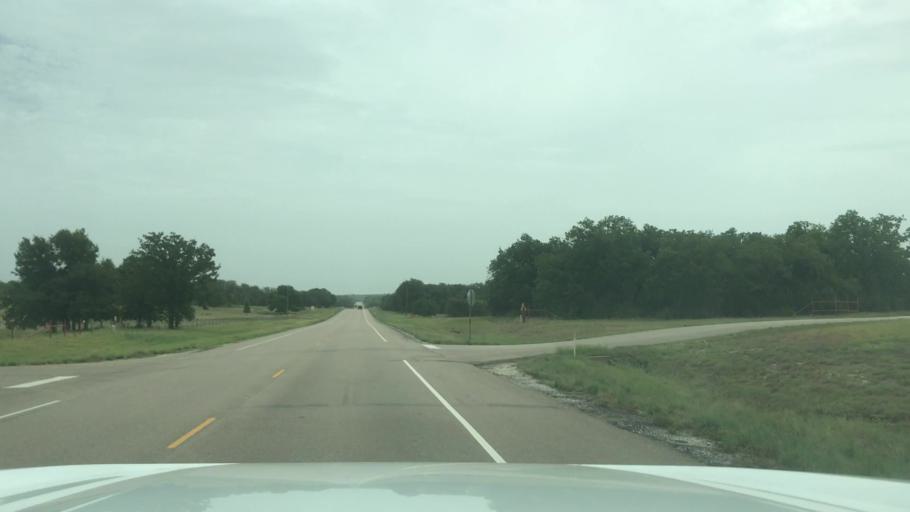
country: US
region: Texas
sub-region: Hamilton County
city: Hico
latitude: 31.9781
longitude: -97.9109
